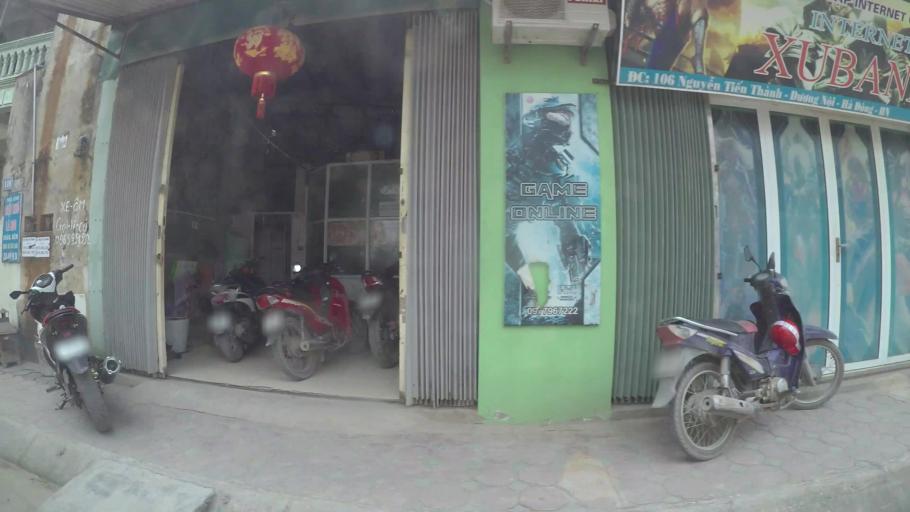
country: VN
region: Ha Noi
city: Ha Dong
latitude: 20.9907
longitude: 105.7418
